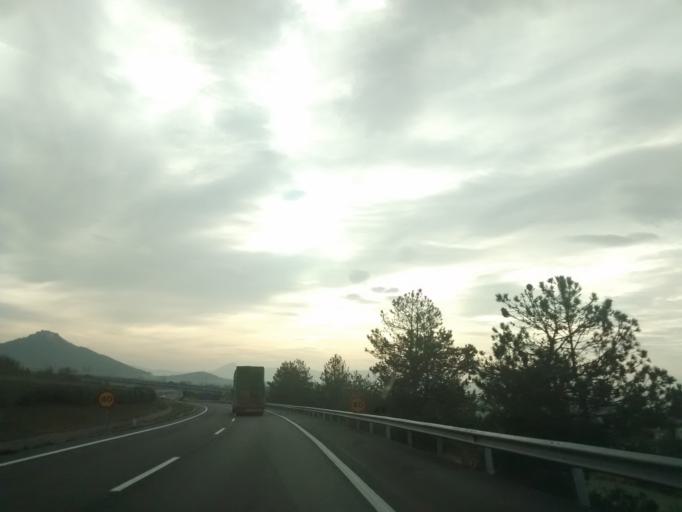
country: ES
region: Navarre
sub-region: Provincia de Navarra
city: Oltza
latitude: 42.8822
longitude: -1.7650
